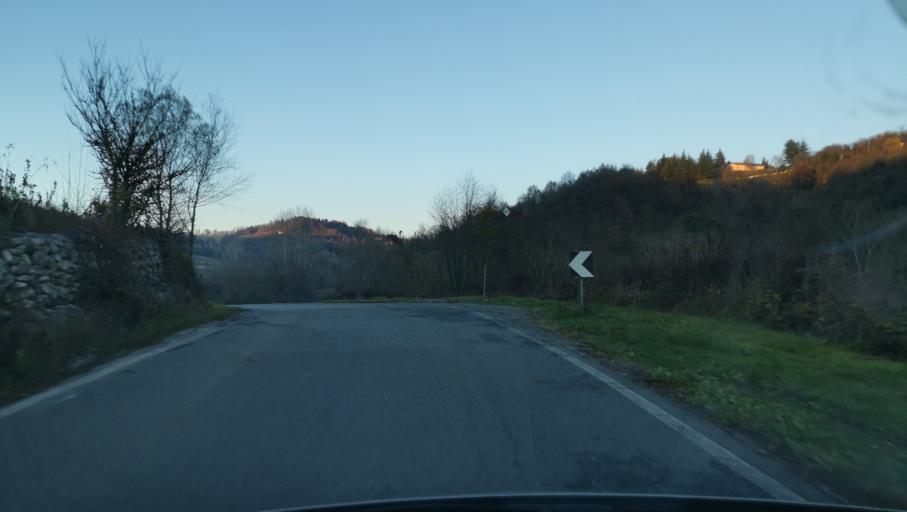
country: IT
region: Piedmont
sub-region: Provincia di Asti
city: Moncucco Torinese
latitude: 45.0749
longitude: 7.9412
